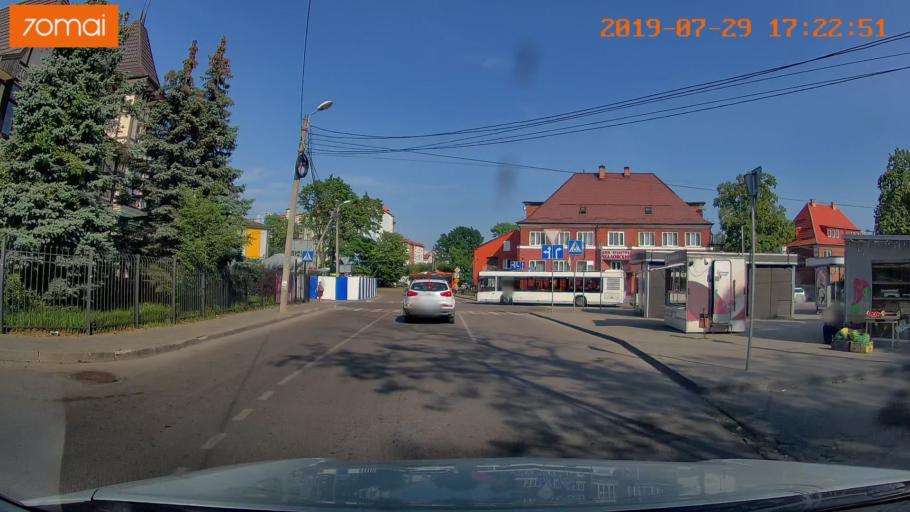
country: RU
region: Kaliningrad
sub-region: Gorod Kaliningrad
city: Kaliningrad
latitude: 54.7681
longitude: 20.4469
